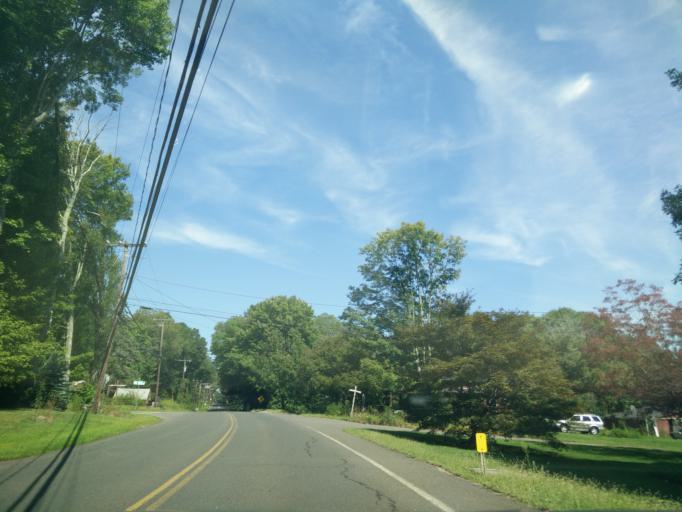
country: US
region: Connecticut
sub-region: New Haven County
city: Madison
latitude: 41.3724
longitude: -72.5648
